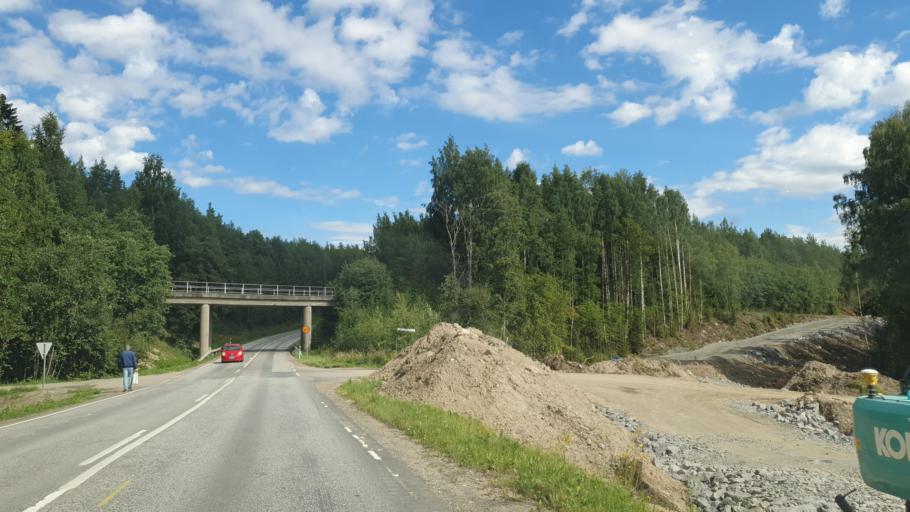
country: FI
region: Central Finland
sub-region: Jyvaeskylae
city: Muurame
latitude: 62.1452
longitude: 25.7107
